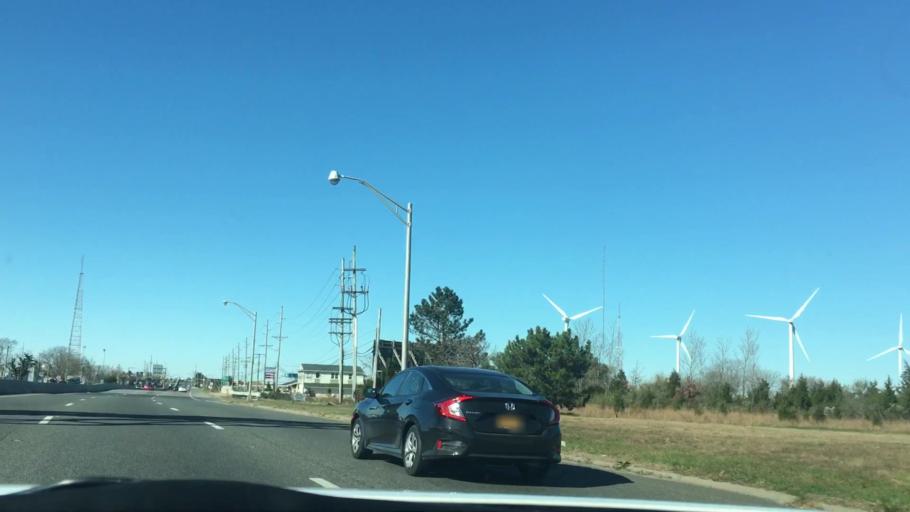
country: US
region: New Jersey
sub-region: Atlantic County
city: Atlantic City
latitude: 39.3745
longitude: -74.4424
